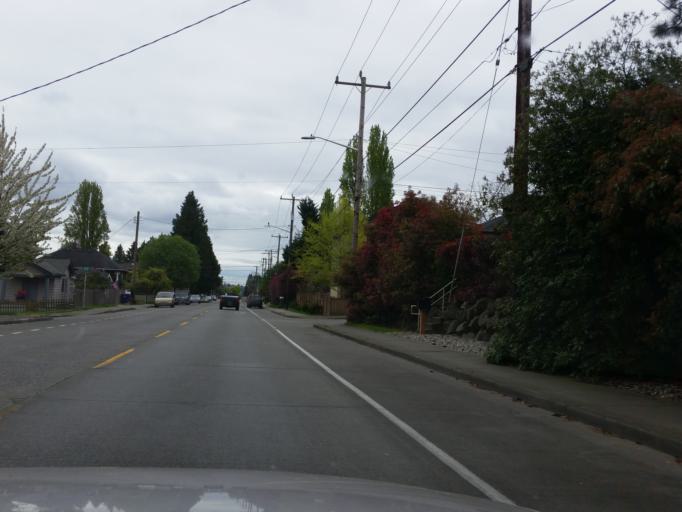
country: US
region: Washington
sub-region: King County
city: Shoreline
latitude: 47.6933
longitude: -122.3661
